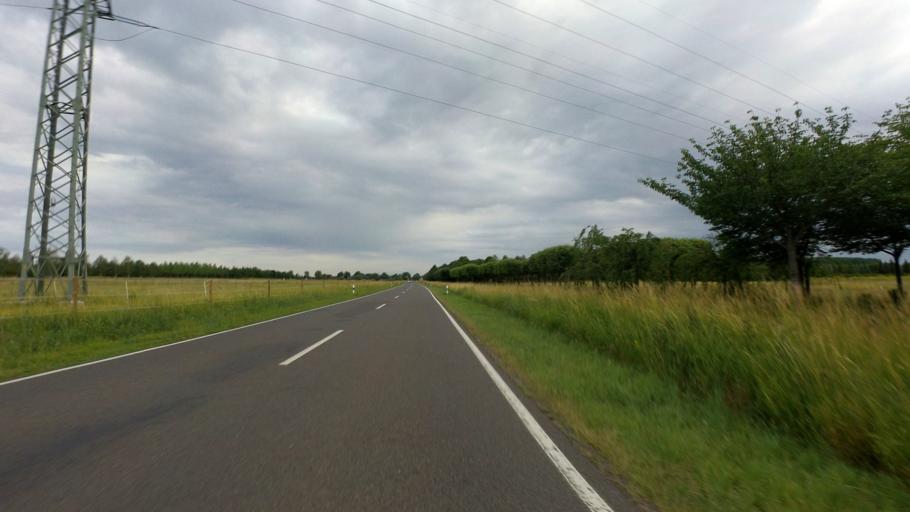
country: DE
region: Brandenburg
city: Pawesin
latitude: 52.5528
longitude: 12.7662
